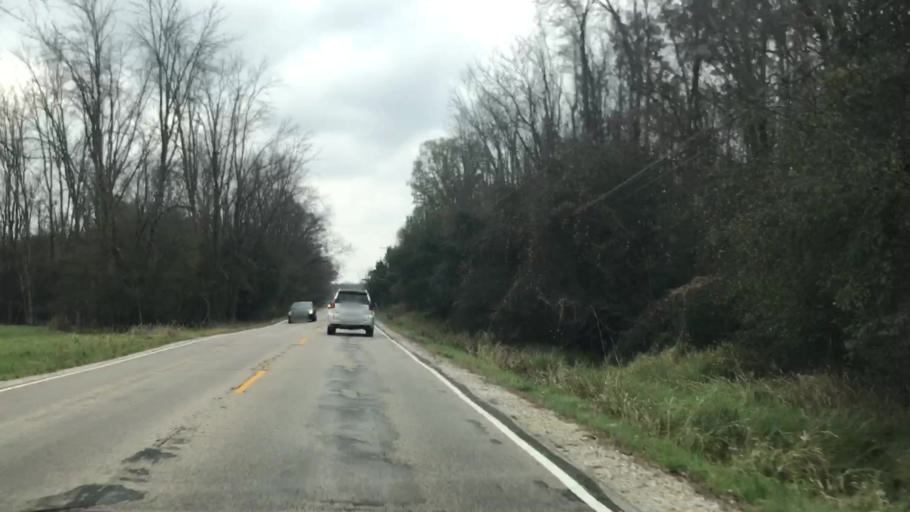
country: US
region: Wisconsin
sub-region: Waukesha County
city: Menomonee Falls
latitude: 43.2029
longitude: -88.1427
